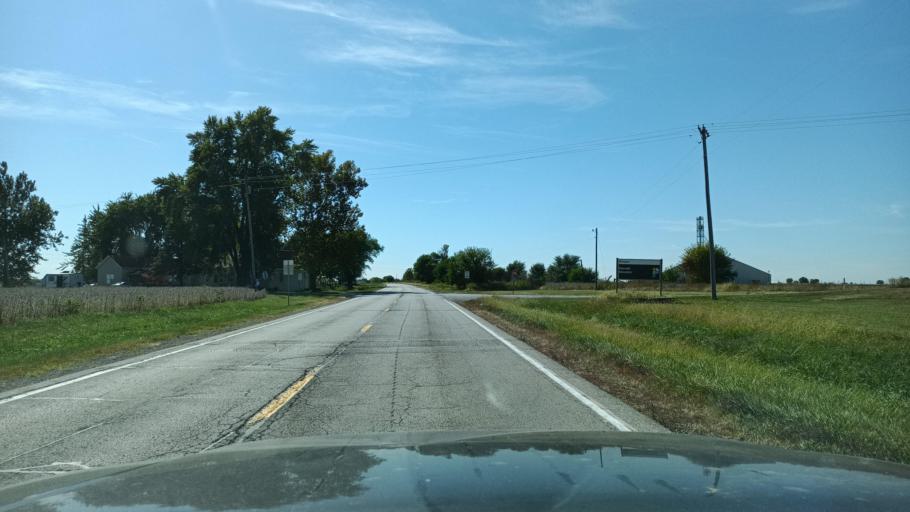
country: US
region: Illinois
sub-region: De Witt County
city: Farmer City
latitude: 40.2221
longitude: -88.7199
